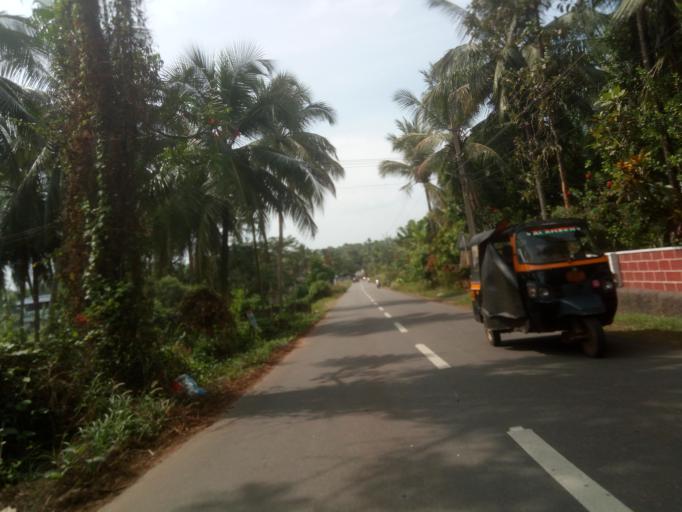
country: IN
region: Kerala
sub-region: Malappuram
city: Ponnani
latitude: 10.7749
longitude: 76.0215
